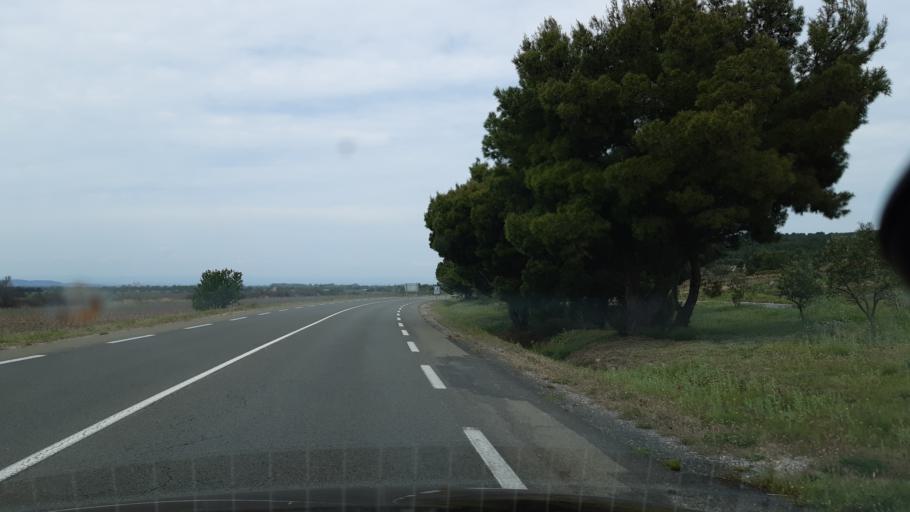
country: FR
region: Languedoc-Roussillon
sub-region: Departement de l'Aude
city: Gruissan
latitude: 43.1334
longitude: 3.0528
